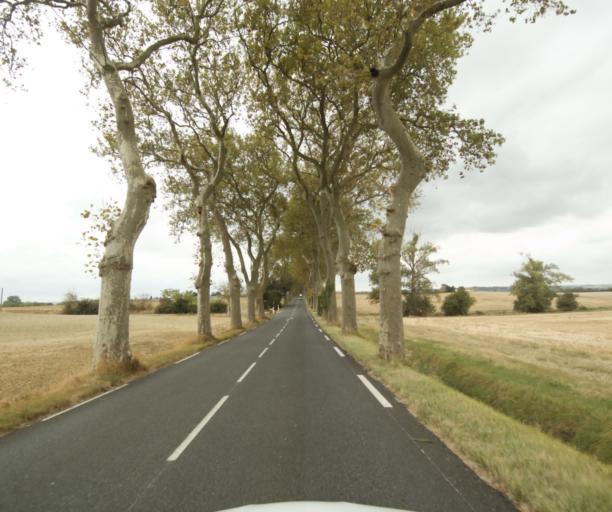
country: FR
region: Midi-Pyrenees
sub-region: Departement de la Haute-Garonne
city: Villefranche-de-Lauragais
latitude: 43.4081
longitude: 1.7314
